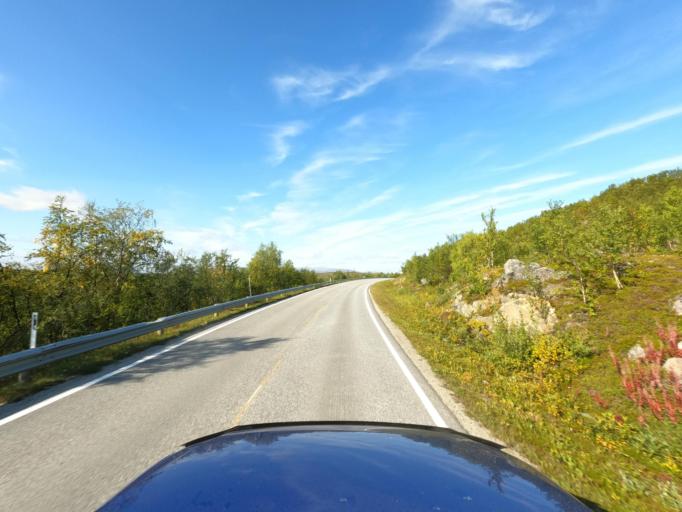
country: NO
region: Finnmark Fylke
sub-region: Porsanger
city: Lakselv
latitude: 69.7682
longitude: 25.1699
